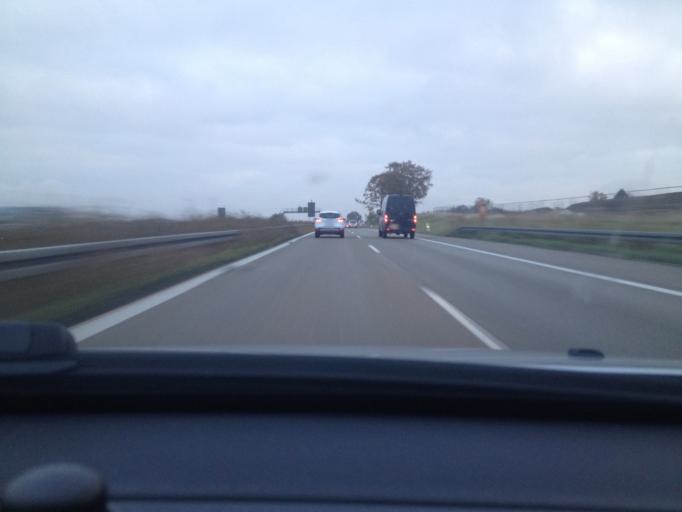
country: DE
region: Baden-Wuerttemberg
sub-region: Tuebingen Region
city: Merklingen
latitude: 48.5227
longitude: 9.7370
